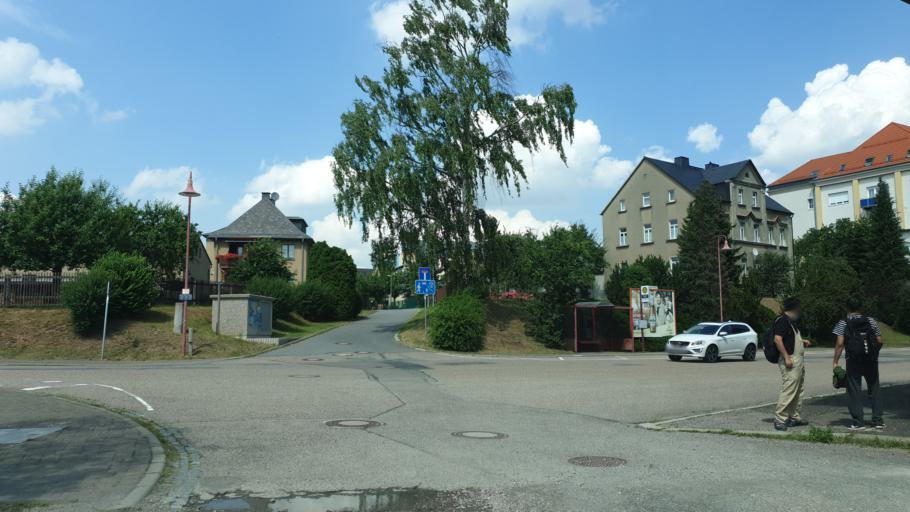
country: DE
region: Saxony
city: Hohenstein-Ernstthal
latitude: 50.8057
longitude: 12.7559
